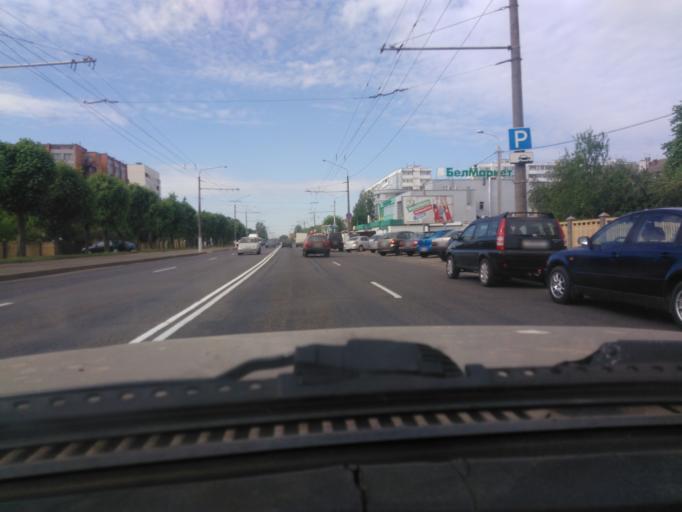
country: BY
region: Mogilev
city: Buynichy
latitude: 53.8865
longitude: 30.2764
